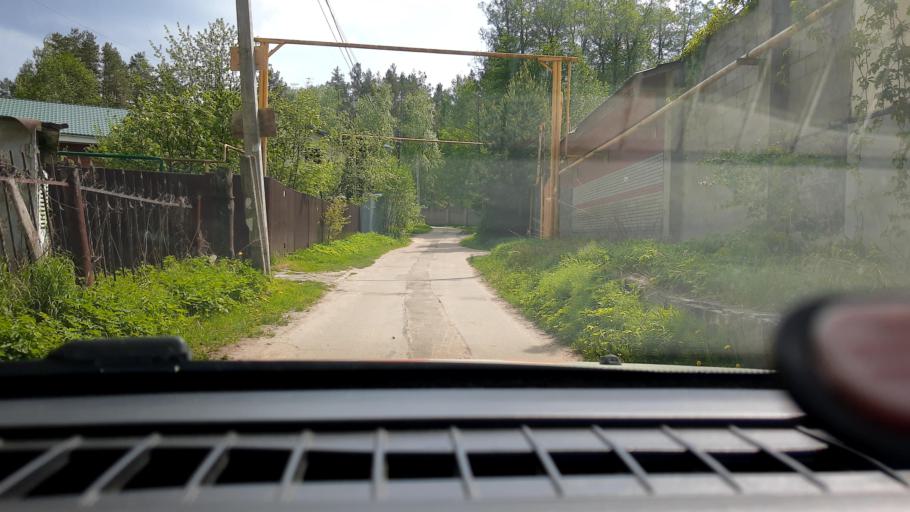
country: RU
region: Nizjnij Novgorod
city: Afonino
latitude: 56.1860
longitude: 44.1004
